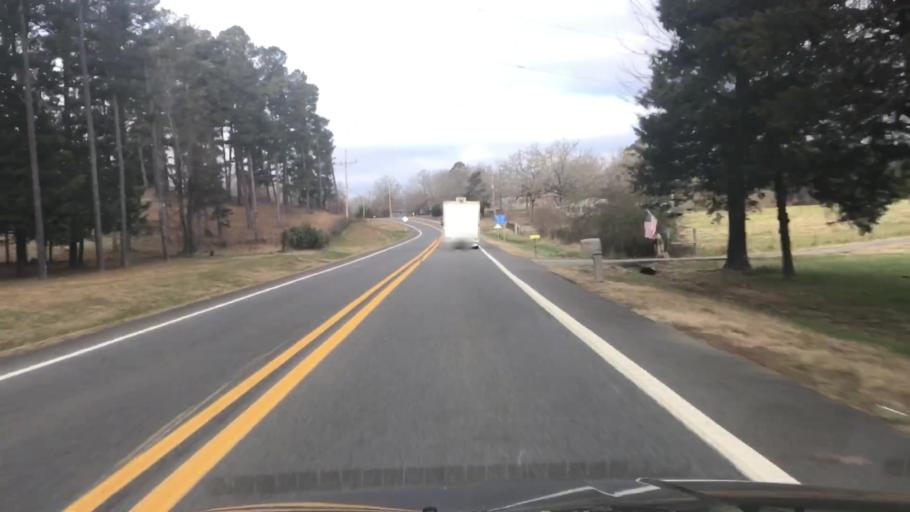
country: US
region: Arkansas
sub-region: Montgomery County
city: Mount Ida
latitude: 34.6227
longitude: -93.7253
